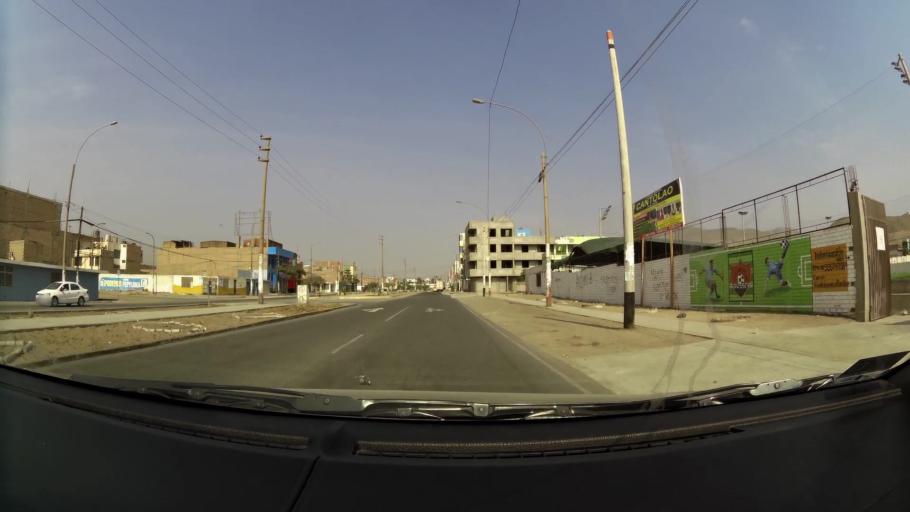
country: PE
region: Lima
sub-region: Lima
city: Santa Rosa
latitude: -11.7834
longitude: -77.1587
